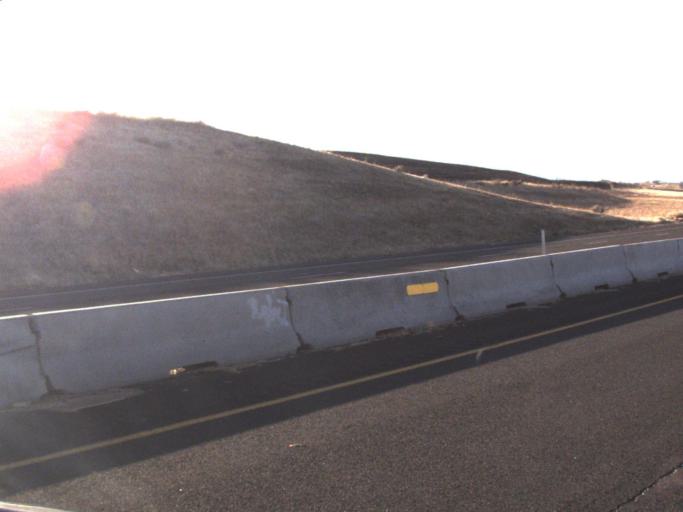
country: US
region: Washington
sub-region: Walla Walla County
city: College Place
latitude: 46.0728
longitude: -118.3795
